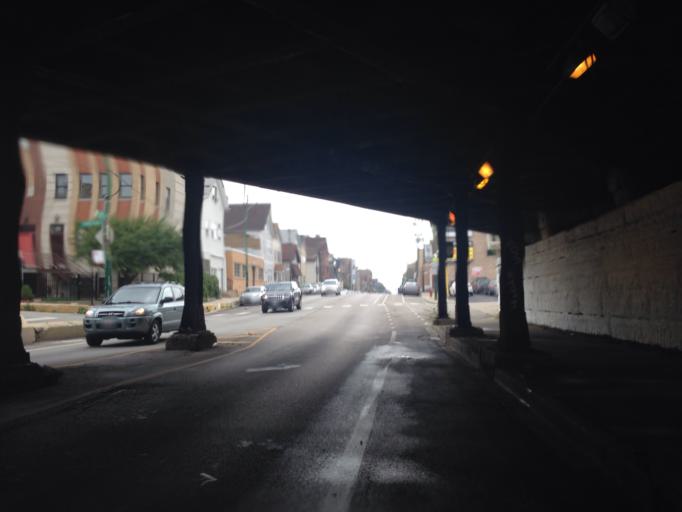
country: US
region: Illinois
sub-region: Cook County
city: Chicago
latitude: 41.9276
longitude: -87.6729
